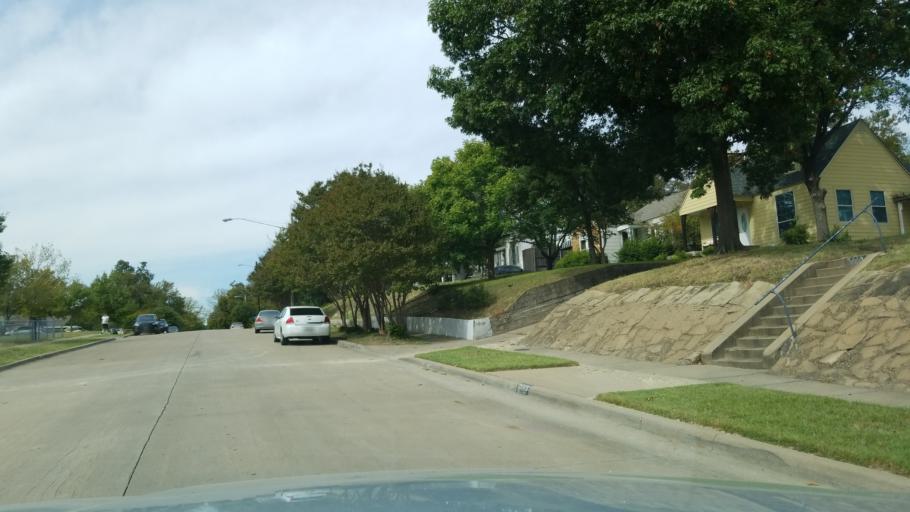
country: US
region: Texas
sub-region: Dallas County
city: Dallas
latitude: 32.7894
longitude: -96.7355
